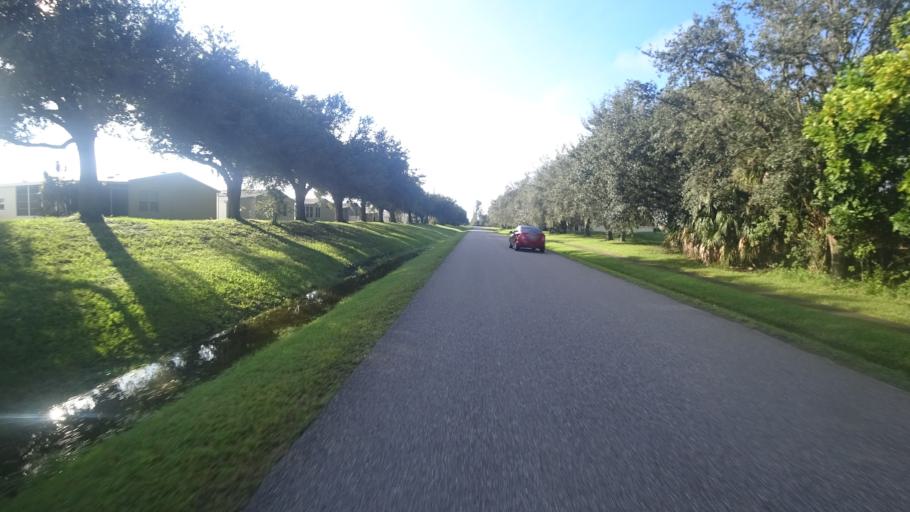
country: US
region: Florida
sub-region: Manatee County
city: Ellenton
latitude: 27.5455
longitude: -82.4663
